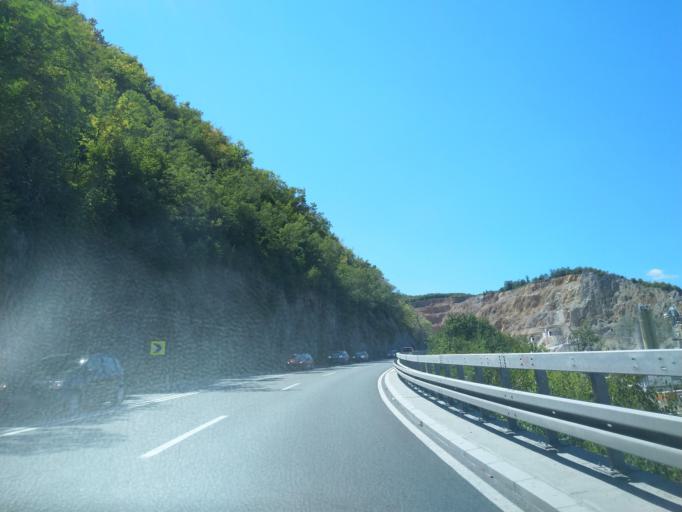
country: RS
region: Central Serbia
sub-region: Zlatiborski Okrug
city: Uzice
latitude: 43.8431
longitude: 19.8161
